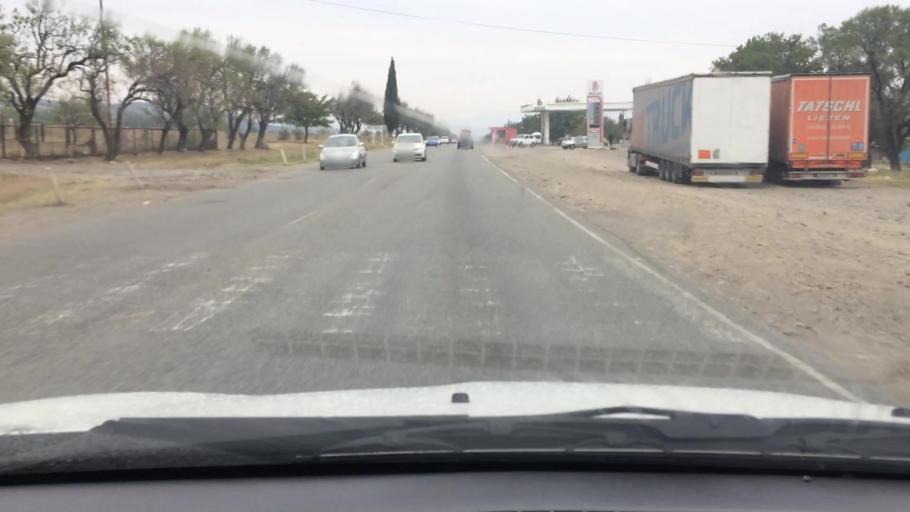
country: GE
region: T'bilisi
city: Tbilisi
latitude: 41.6325
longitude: 44.8152
